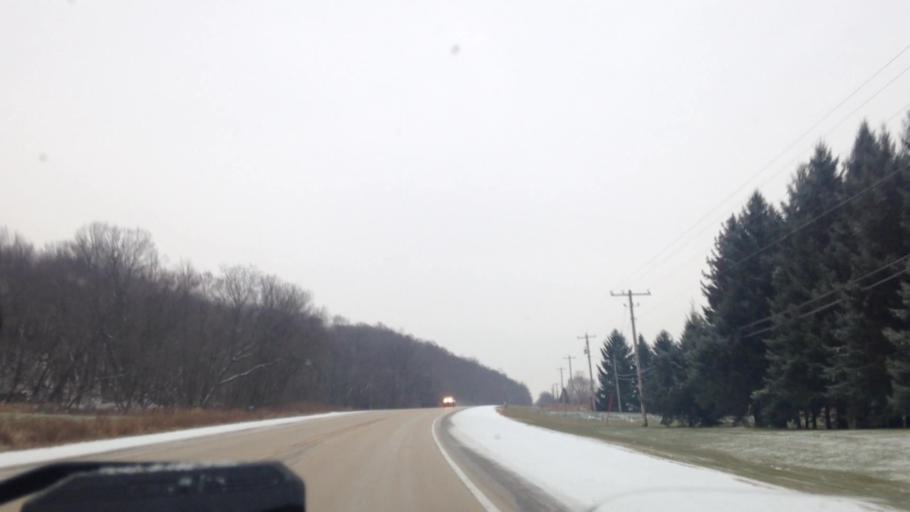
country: US
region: Wisconsin
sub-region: Dodge County
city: Mayville
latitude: 43.4551
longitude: -88.5422
